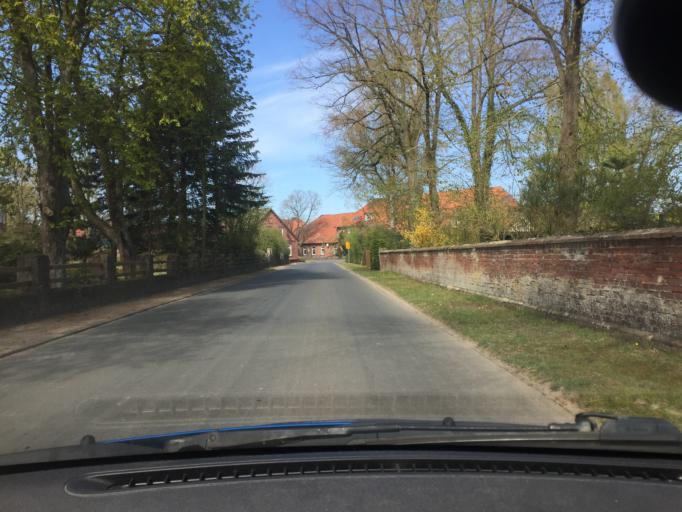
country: DE
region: Lower Saxony
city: Ratzlingen
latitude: 52.9566
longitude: 10.6691
